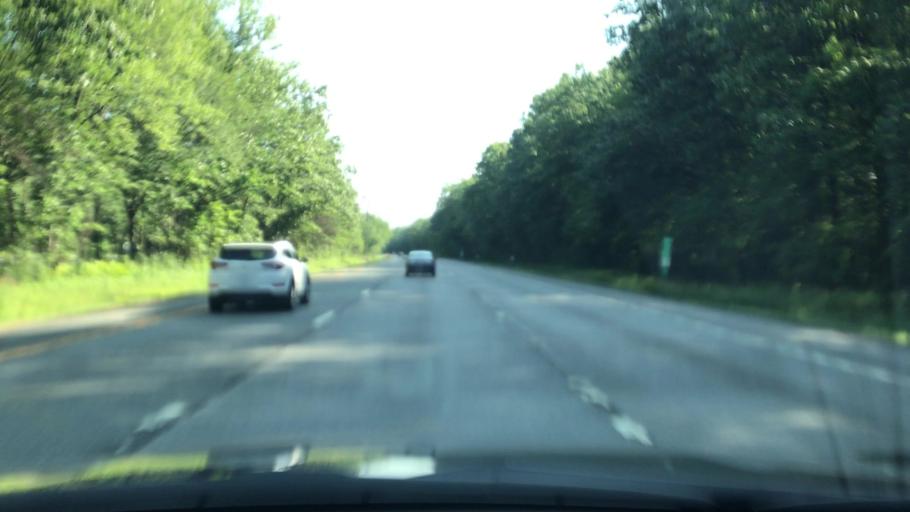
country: US
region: New York
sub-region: Saratoga County
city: Saratoga Springs
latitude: 43.1591
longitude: -73.7209
